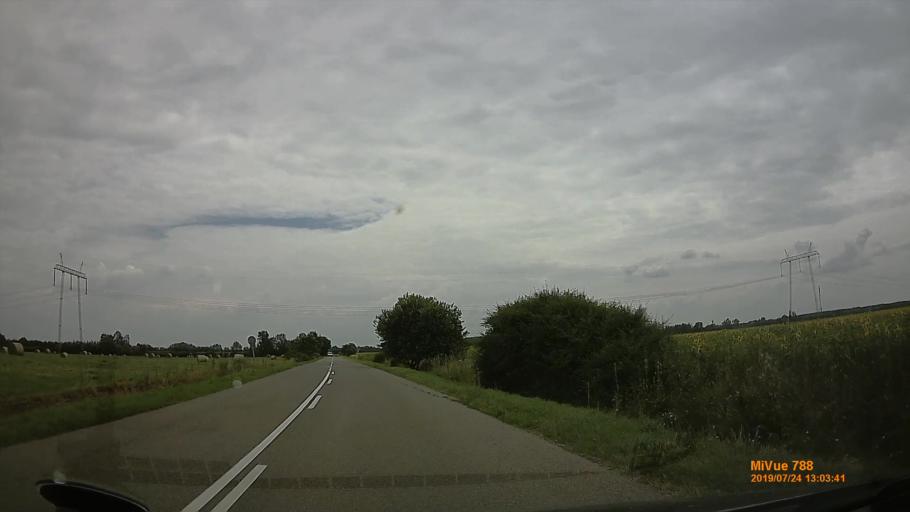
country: HU
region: Szabolcs-Szatmar-Bereg
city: Aranyosapati
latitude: 48.2091
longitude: 22.3003
